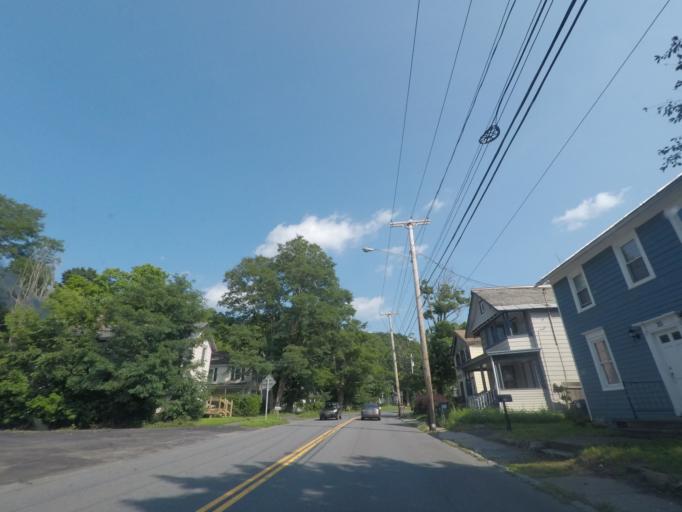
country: US
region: New York
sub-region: Rensselaer County
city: Nassau
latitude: 42.5152
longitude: -73.6074
